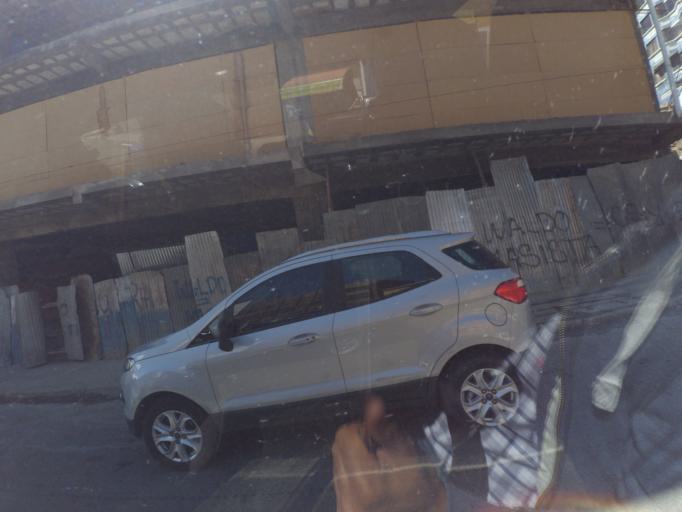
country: BO
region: La Paz
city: La Paz
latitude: -16.4933
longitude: -68.1470
